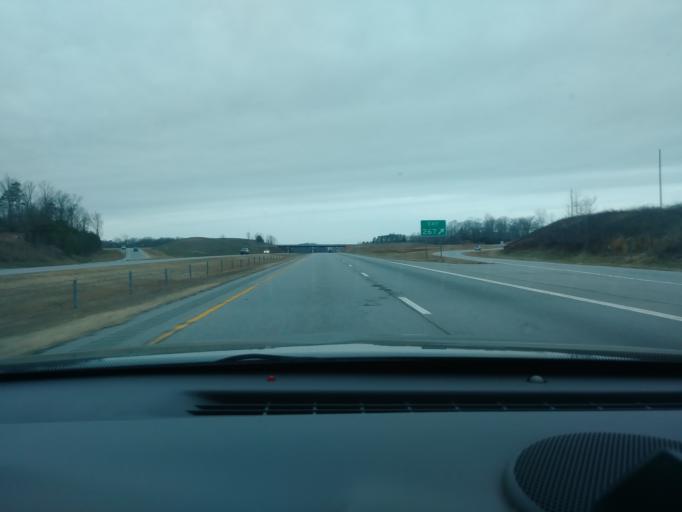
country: US
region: North Carolina
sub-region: Yadkin County
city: Jonesville
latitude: 36.1292
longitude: -80.8376
